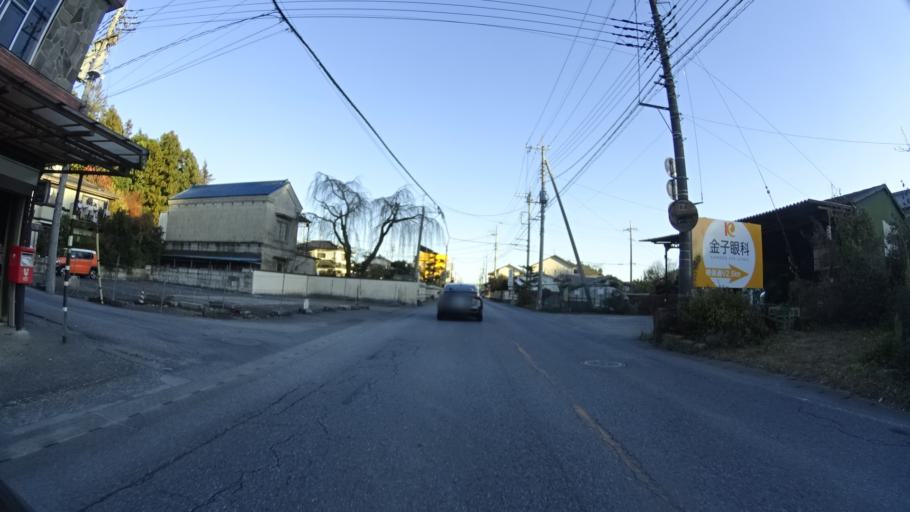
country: JP
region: Tochigi
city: Utsunomiya-shi
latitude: 36.5855
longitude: 139.8323
